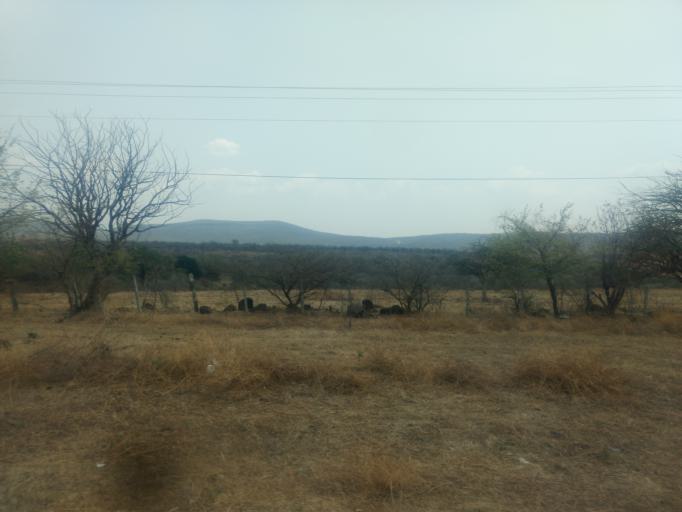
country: MX
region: Morelos
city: La Joya
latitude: 18.6700
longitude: -99.4293
